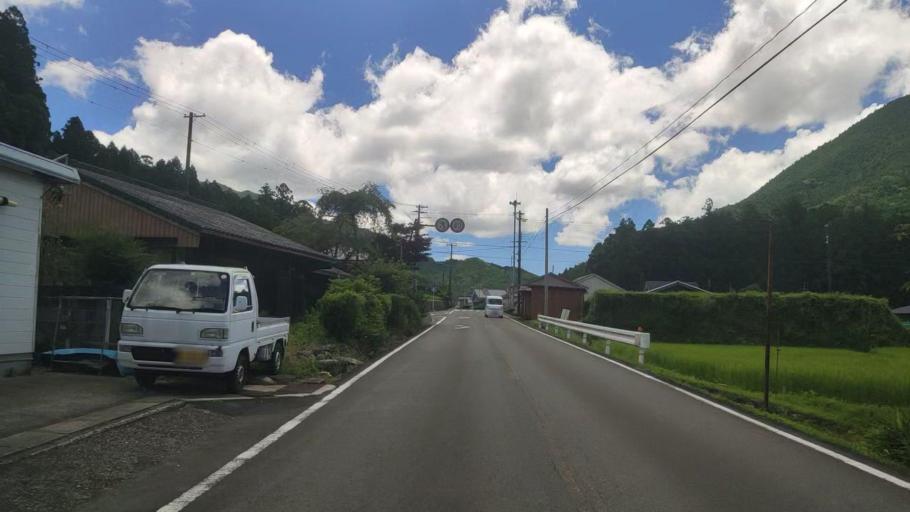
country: JP
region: Mie
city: Owase
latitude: 33.9786
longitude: 136.0519
